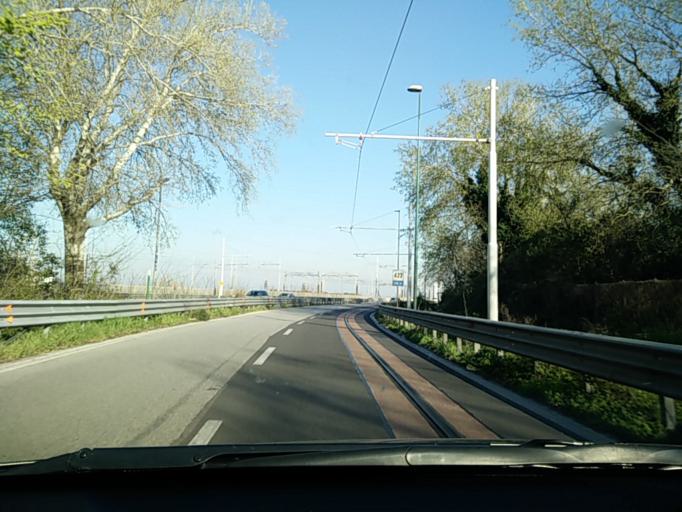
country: IT
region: Veneto
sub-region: Provincia di Venezia
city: Campalto
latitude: 45.4652
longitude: 12.2776
